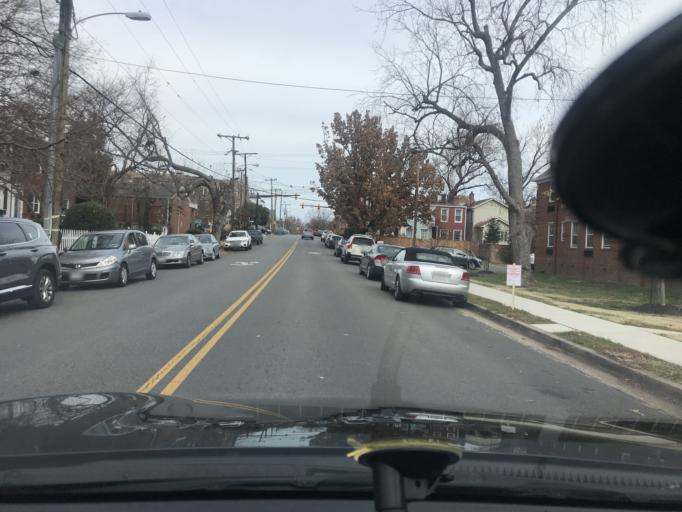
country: US
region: Virginia
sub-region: City of Alexandria
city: Alexandria
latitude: 38.7975
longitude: -77.0498
